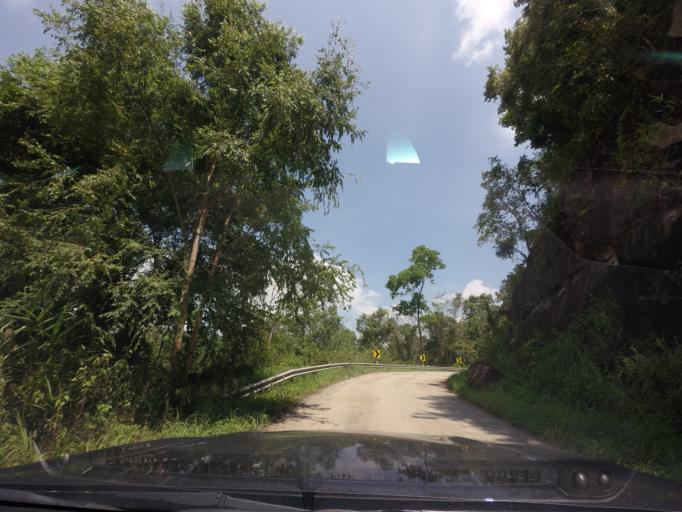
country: TH
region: Loei
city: Na Haeo
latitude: 17.6156
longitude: 100.8971
